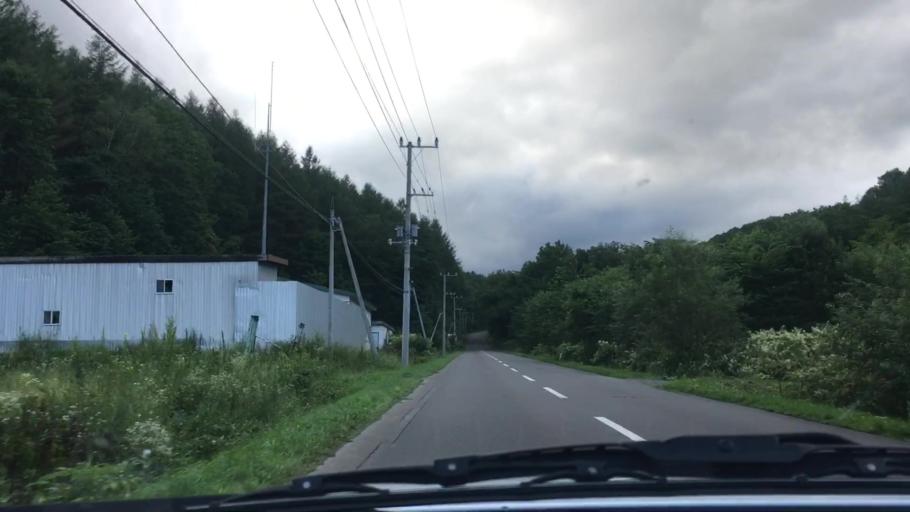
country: JP
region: Hokkaido
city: Otofuke
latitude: 43.1433
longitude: 142.8804
